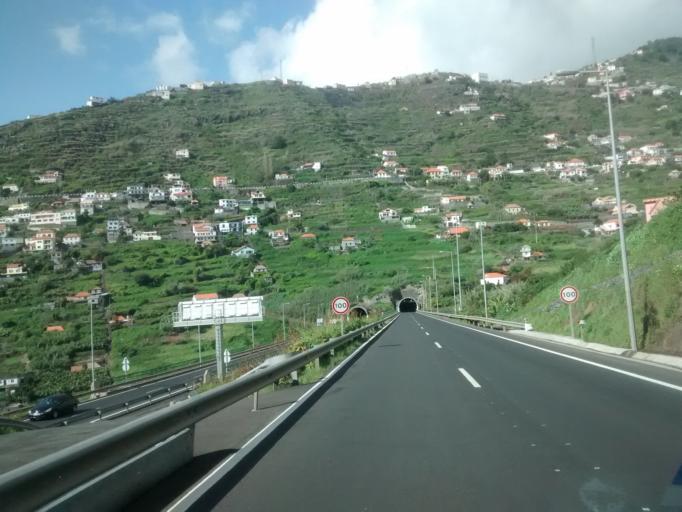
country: PT
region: Madeira
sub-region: Ribeira Brava
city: Campanario
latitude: 32.6666
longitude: -17.0403
